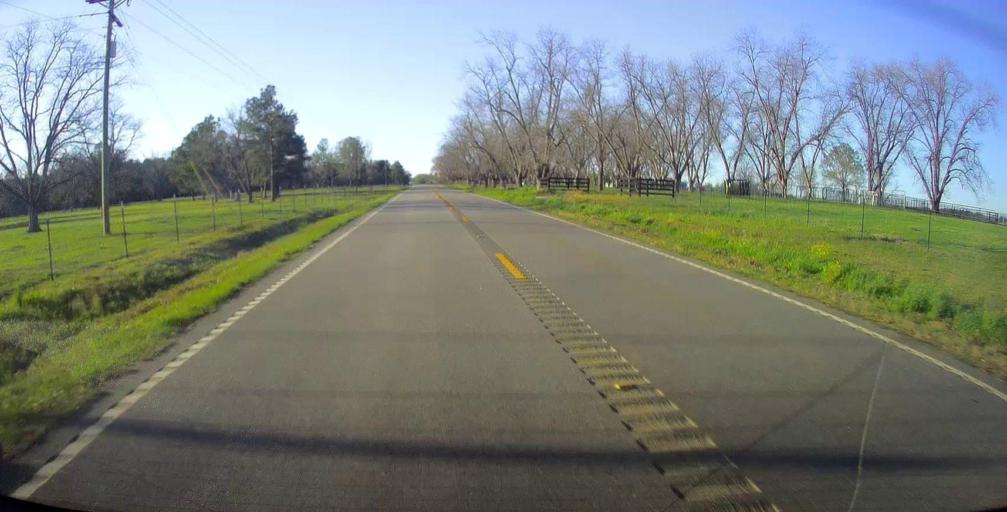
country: US
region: Georgia
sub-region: Wilcox County
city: Abbeville
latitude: 32.1523
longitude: -83.3500
